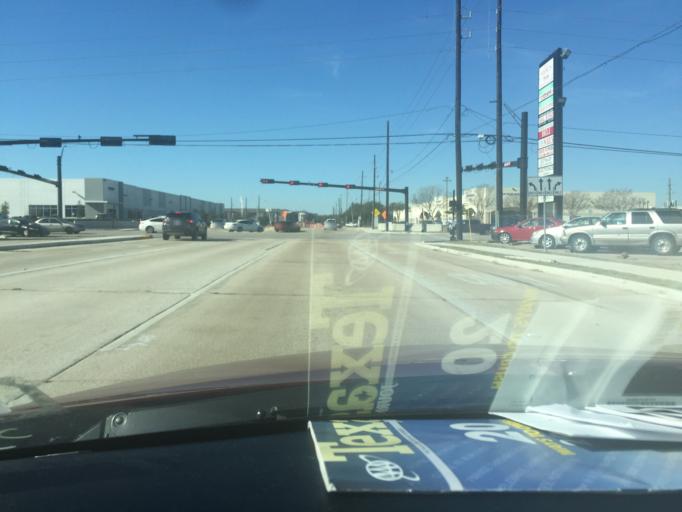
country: US
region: Texas
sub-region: Fort Bend County
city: Meadows Place
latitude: 29.6413
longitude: -95.5646
